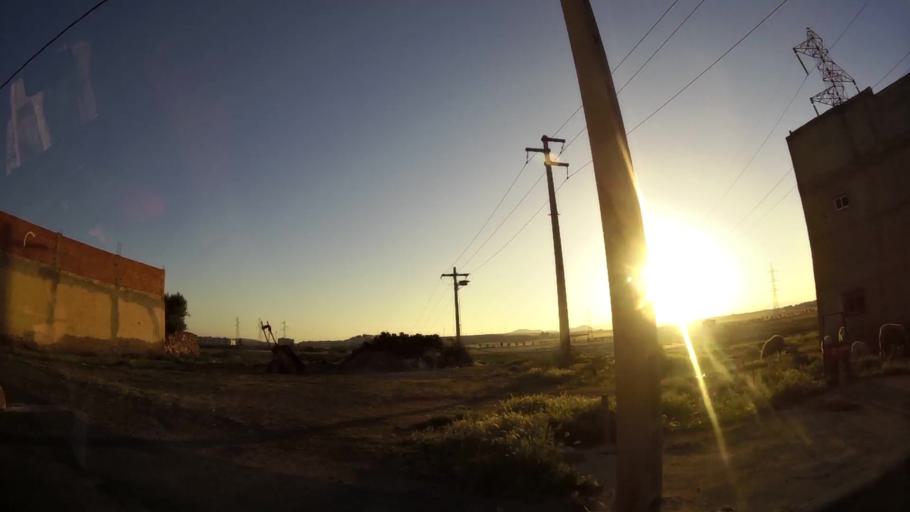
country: MA
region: Oriental
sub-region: Oujda-Angad
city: Oujda
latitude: 34.7089
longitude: -1.9224
